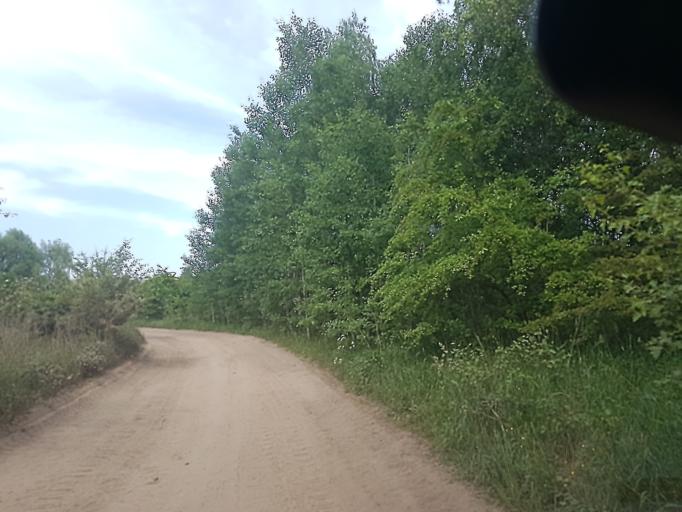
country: DE
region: Brandenburg
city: Gorzke
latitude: 52.1082
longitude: 12.3838
